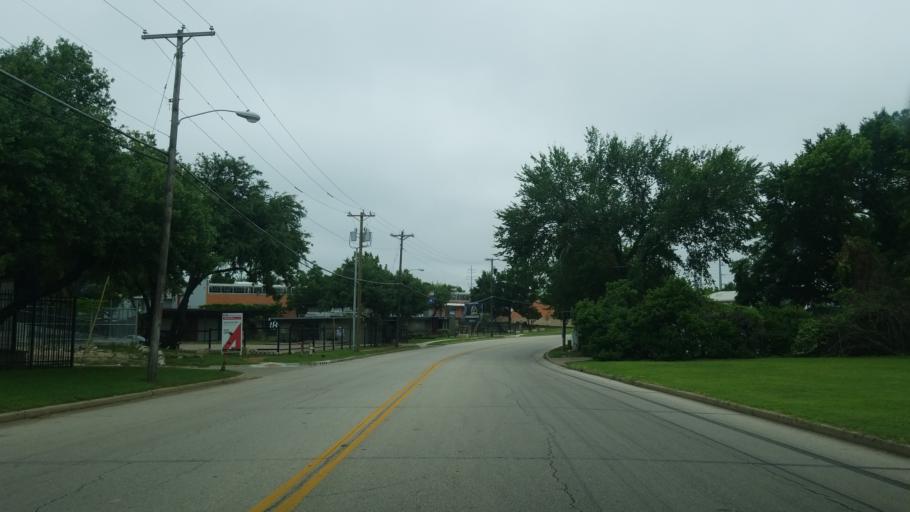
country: US
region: Texas
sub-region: Dallas County
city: University Park
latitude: 32.8437
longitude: -96.8697
